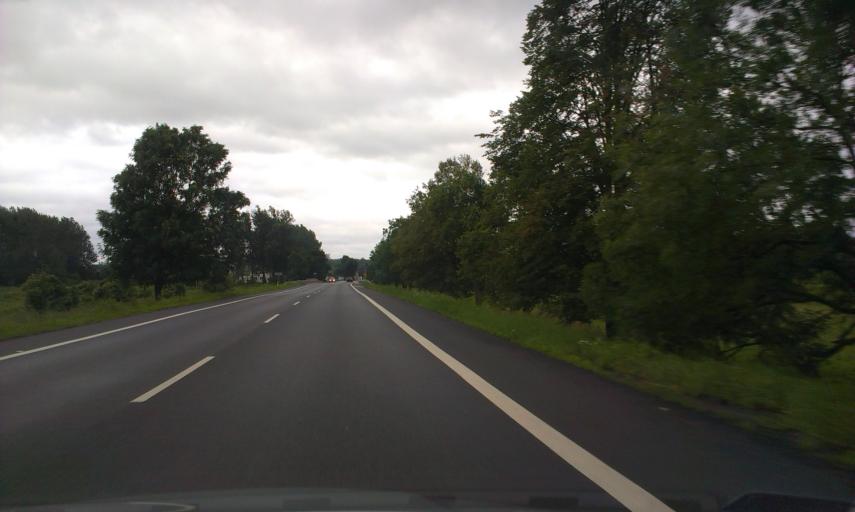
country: PL
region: Greater Poland Voivodeship
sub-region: Powiat pilski
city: Ujscie
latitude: 53.0678
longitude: 16.7307
